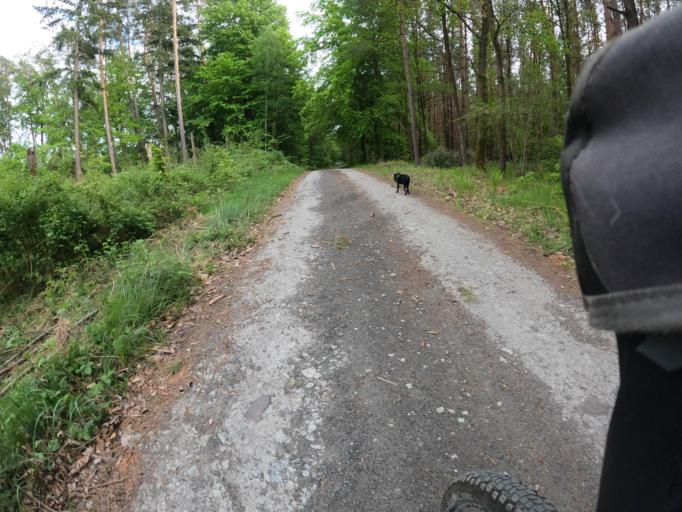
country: PL
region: West Pomeranian Voivodeship
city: Trzcinsko Zdroj
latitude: 52.9107
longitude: 14.6885
